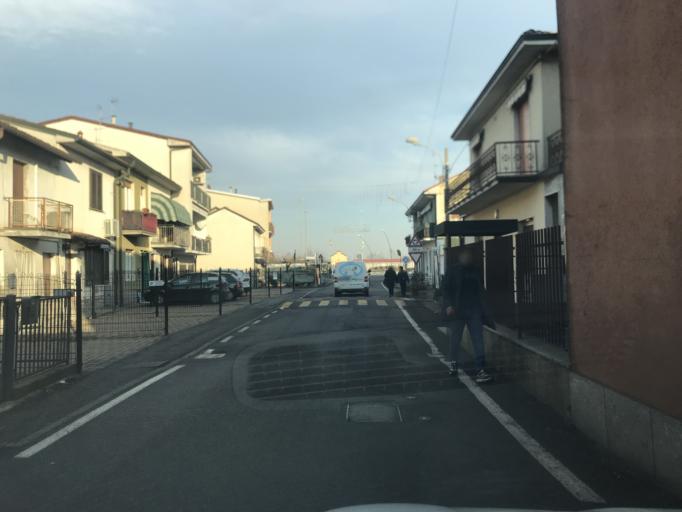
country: IT
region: Lombardy
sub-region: Provincia di Lodi
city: Borgo San Giovanni
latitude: 45.2787
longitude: 9.4382
